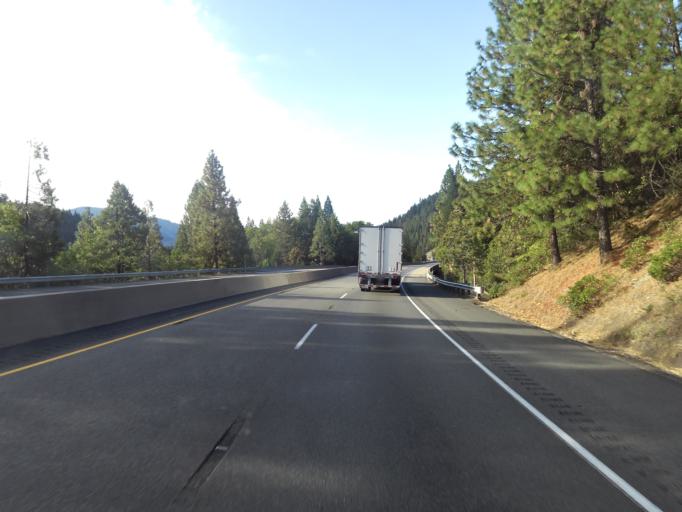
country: US
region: California
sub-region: Siskiyou County
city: Dunsmuir
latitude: 41.2006
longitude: -122.2783
